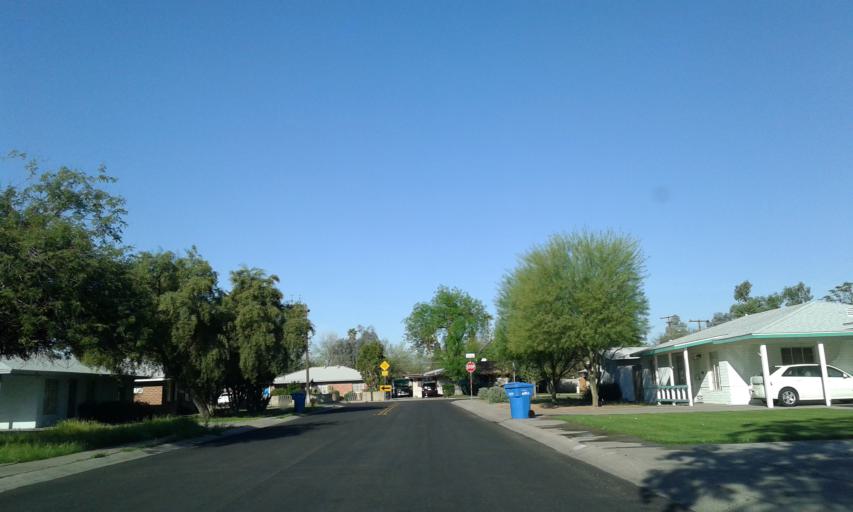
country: US
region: Arizona
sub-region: Maricopa County
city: Phoenix
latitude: 33.4928
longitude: -112.1069
